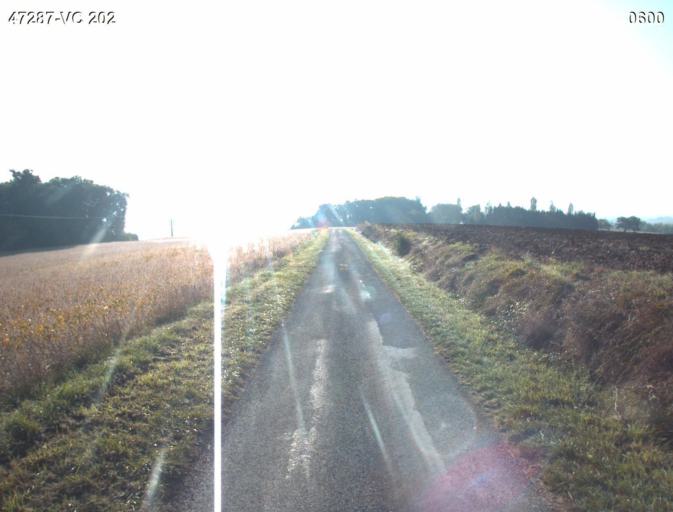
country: FR
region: Aquitaine
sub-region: Departement du Lot-et-Garonne
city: Laplume
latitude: 44.1153
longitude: 0.4641
